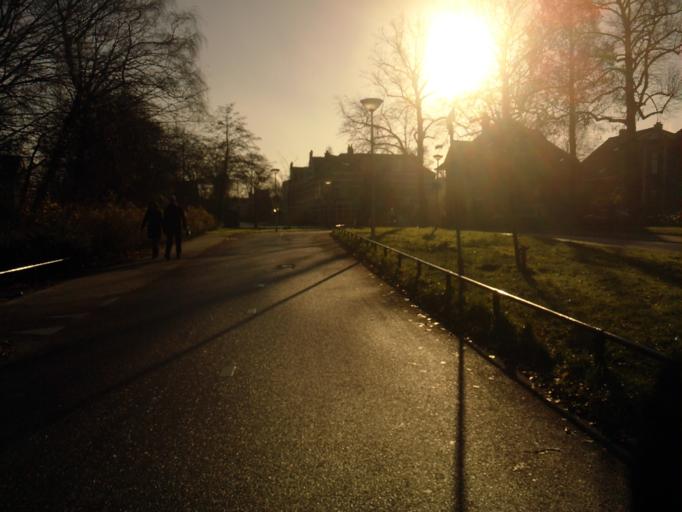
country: NL
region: Utrecht
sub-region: Gemeente Amersfoort
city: Amersfoort
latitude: 52.1613
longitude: 5.3888
